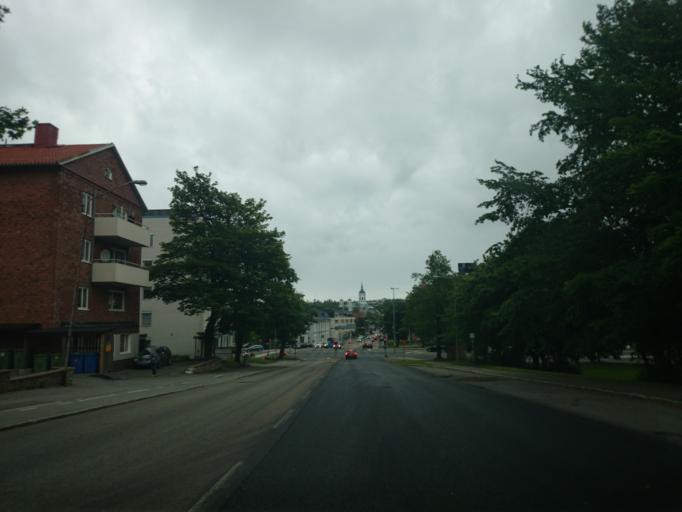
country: SE
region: Vaesternorrland
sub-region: Haernoesands Kommun
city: Haernoesand
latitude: 62.6287
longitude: 17.9297
